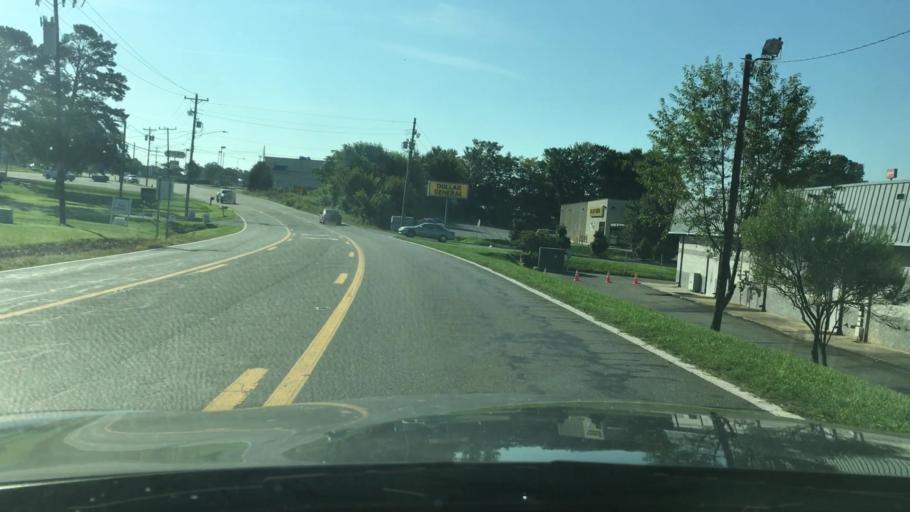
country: US
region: North Carolina
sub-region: Alamance County
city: Burlington
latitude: 36.0682
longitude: -79.4315
